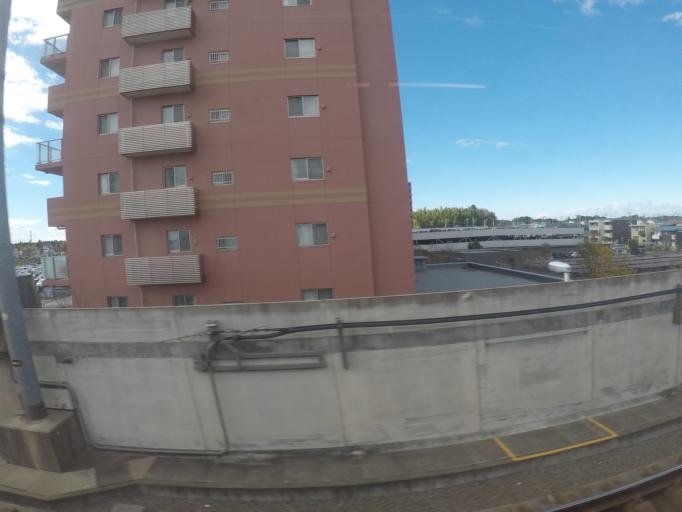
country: JP
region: Ibaraki
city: Mitsukaido
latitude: 36.0601
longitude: 140.0592
